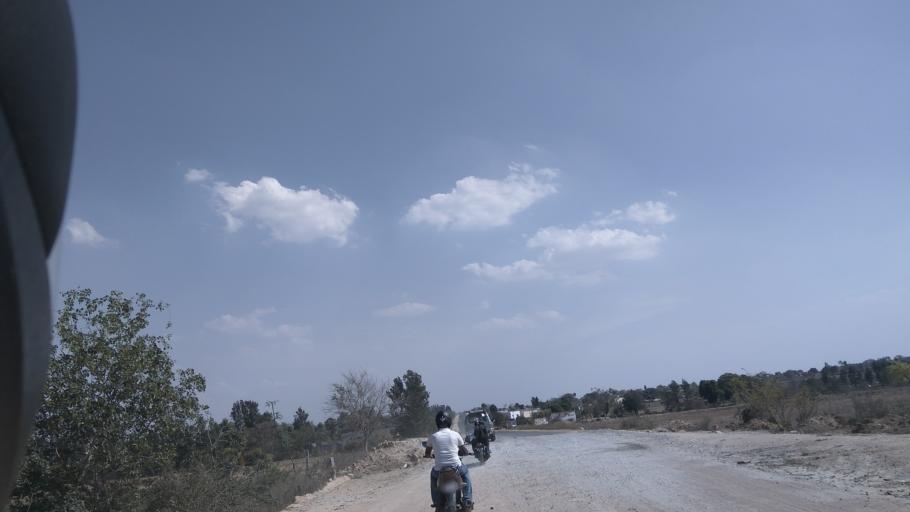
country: IN
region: Karnataka
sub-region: Kolar
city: Mulbagal
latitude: 13.1830
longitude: 78.3512
